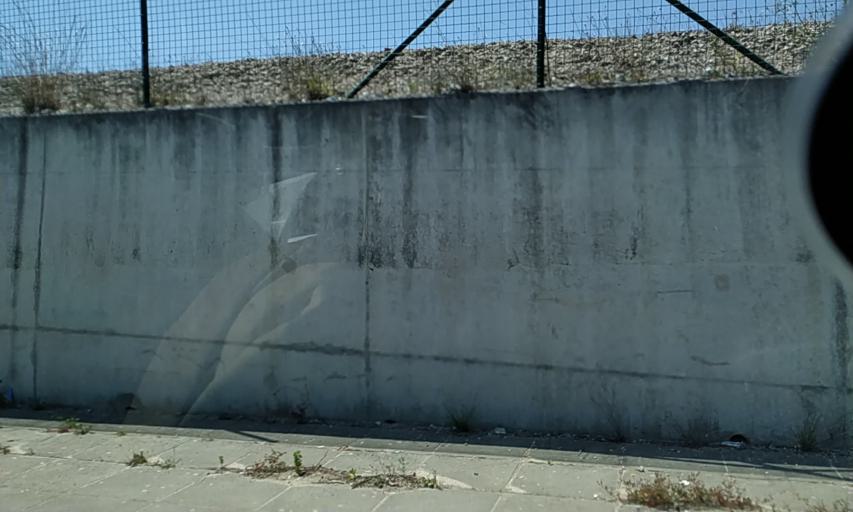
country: PT
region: Setubal
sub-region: Palmela
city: Palmela
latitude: 38.5701
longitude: -8.8723
